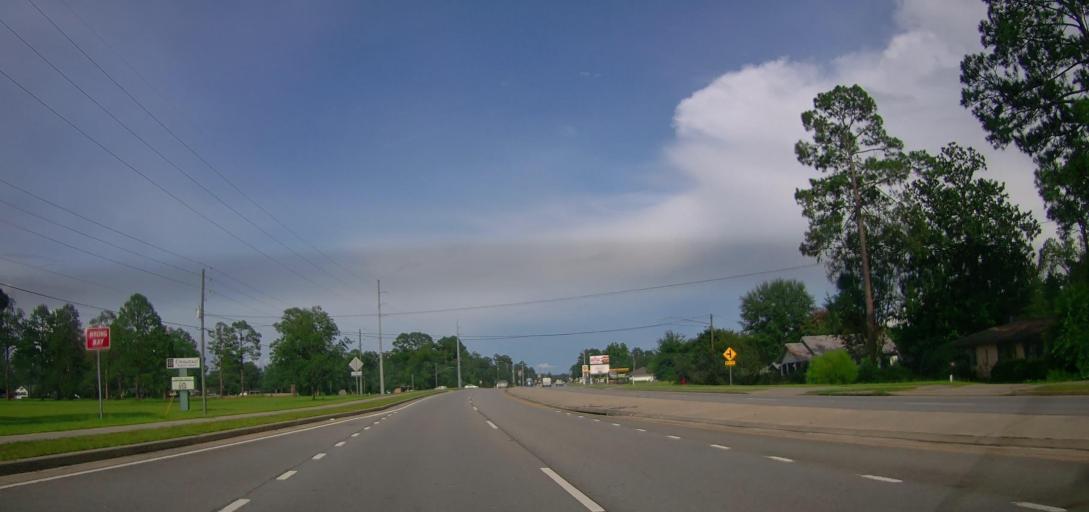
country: US
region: Georgia
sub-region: Wayne County
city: Jesup
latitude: 31.6052
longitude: -81.9183
